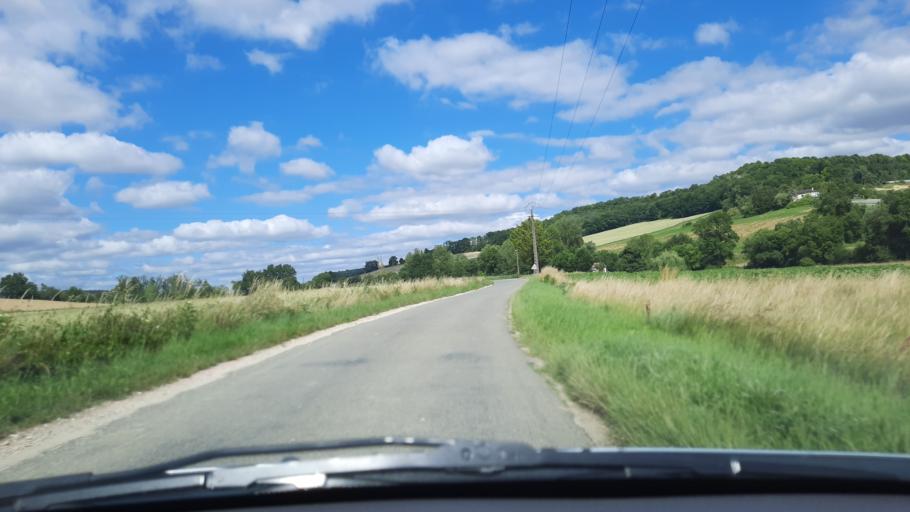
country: FR
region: Midi-Pyrenees
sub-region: Departement du Lot
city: Castelnau-Montratier
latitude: 44.2766
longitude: 1.4009
